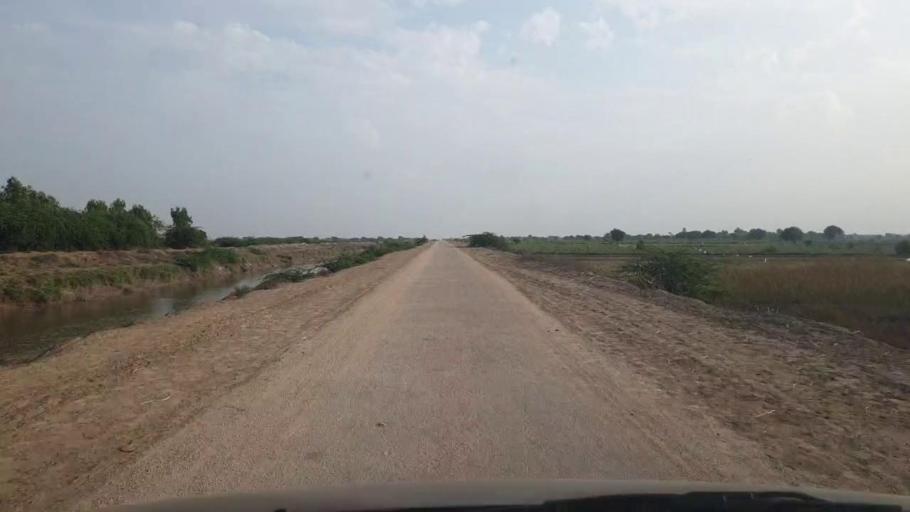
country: PK
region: Sindh
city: Badin
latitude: 24.5462
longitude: 68.6720
